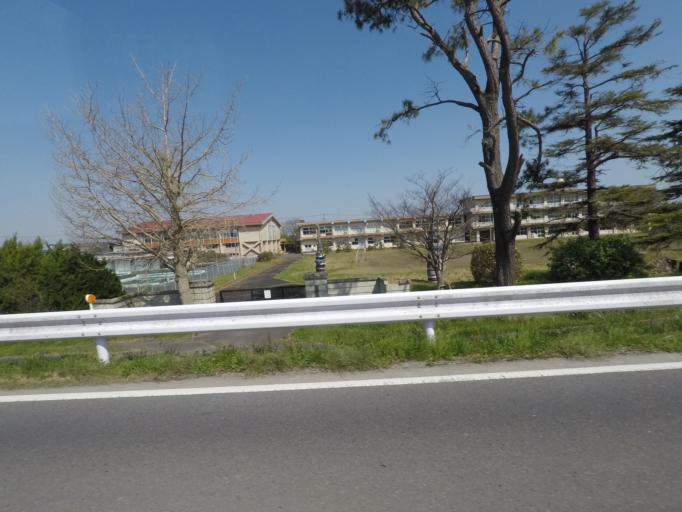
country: JP
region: Chiba
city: Katori-shi
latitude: 35.9098
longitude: 140.4220
